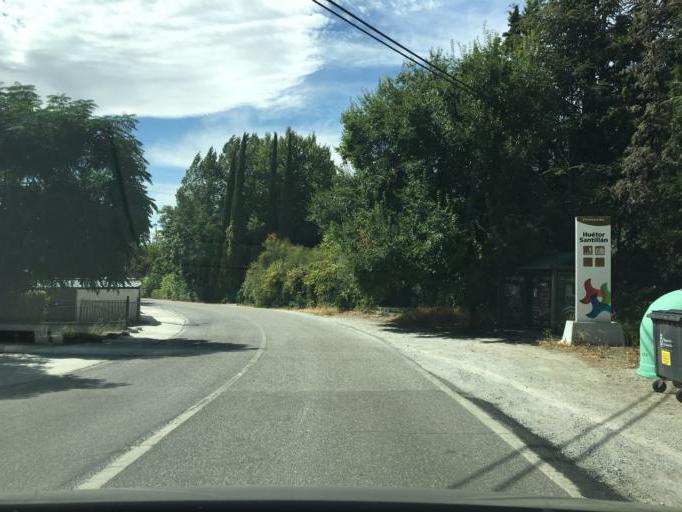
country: ES
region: Andalusia
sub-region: Provincia de Granada
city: Huetor Santillan
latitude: 37.2299
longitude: -3.5002
